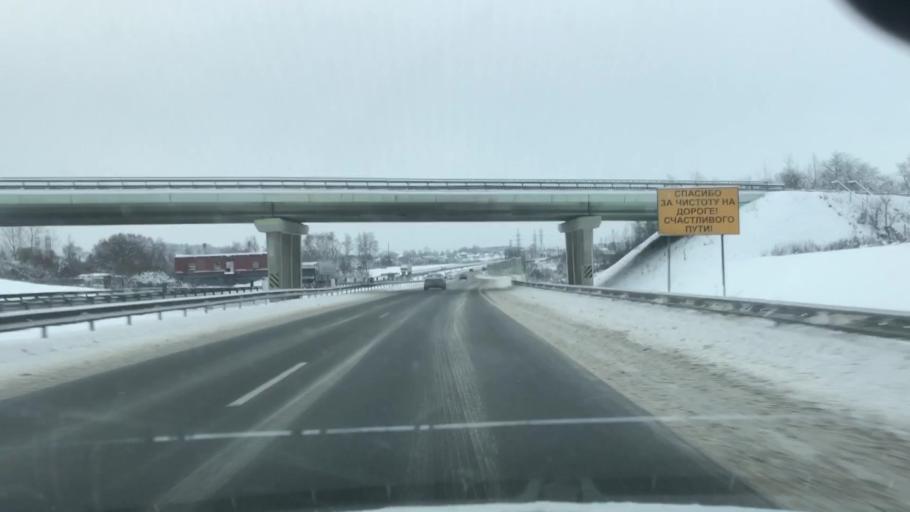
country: RU
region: Moskovskaya
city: Mikhnevo
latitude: 55.1280
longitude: 37.9348
